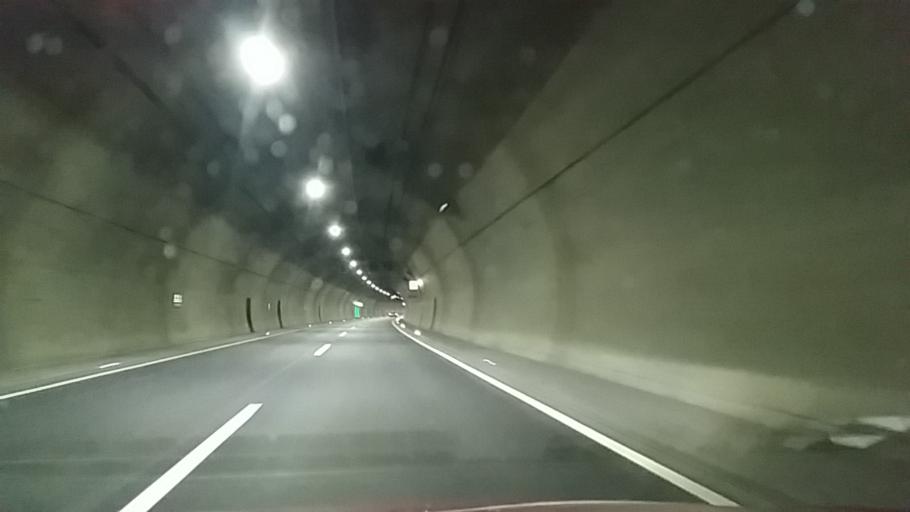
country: DE
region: Thuringia
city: Zella-Mehlis
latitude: 50.6345
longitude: 10.6722
